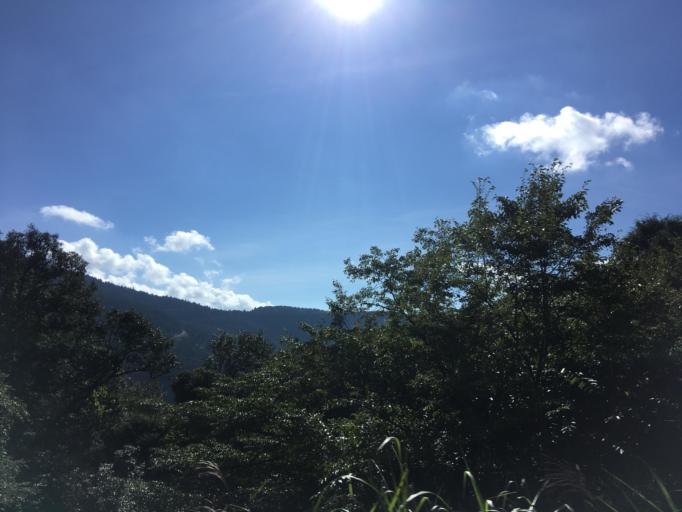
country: TW
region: Taiwan
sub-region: Yilan
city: Yilan
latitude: 24.4953
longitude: 121.5514
